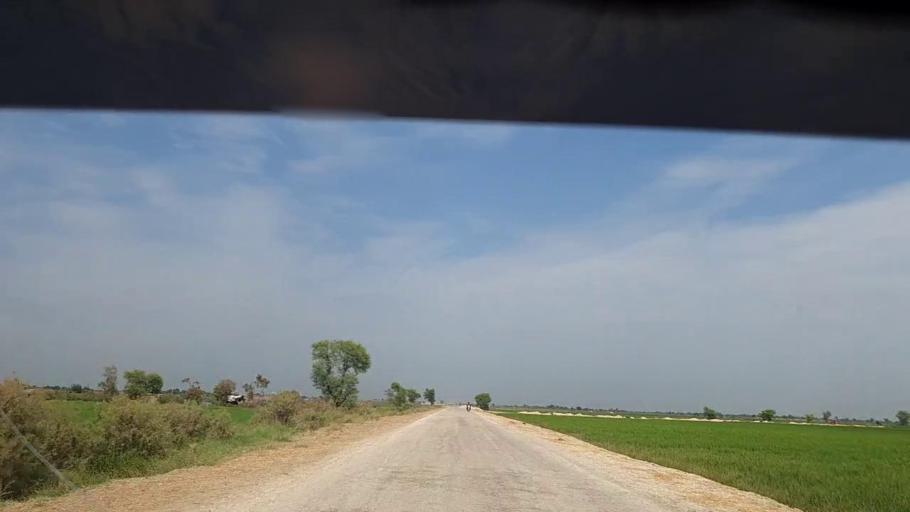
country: PK
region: Sindh
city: Thul
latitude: 28.1945
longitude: 68.7756
